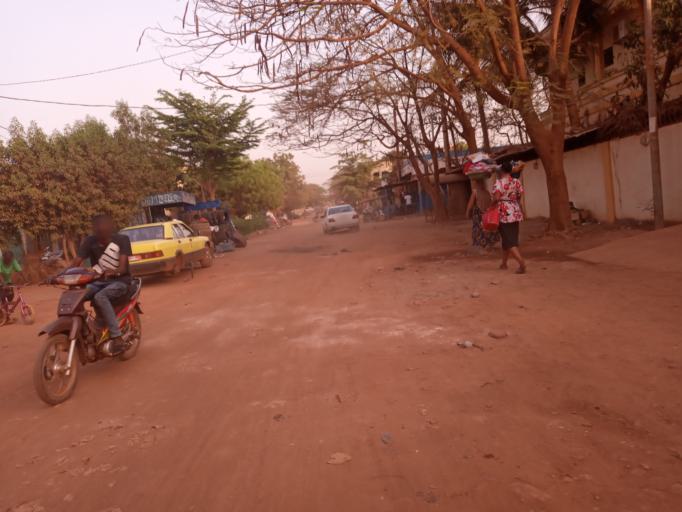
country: ML
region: Bamako
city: Bamako
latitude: 12.5859
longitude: -7.9524
